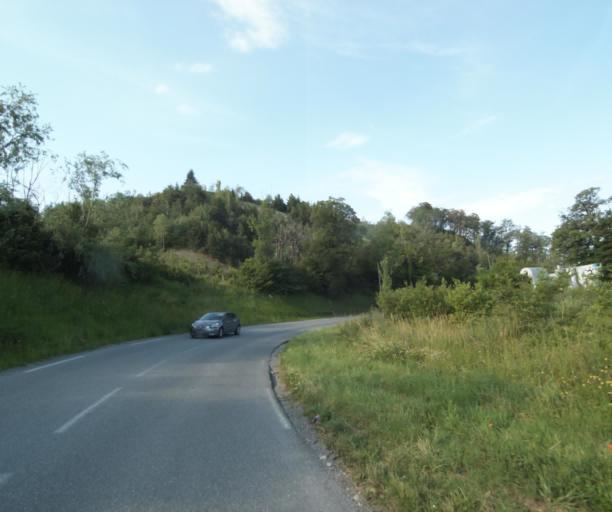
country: FR
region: Rhone-Alpes
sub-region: Departement de la Haute-Savoie
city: Thonon-les-Bains
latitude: 46.3629
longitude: 6.4959
